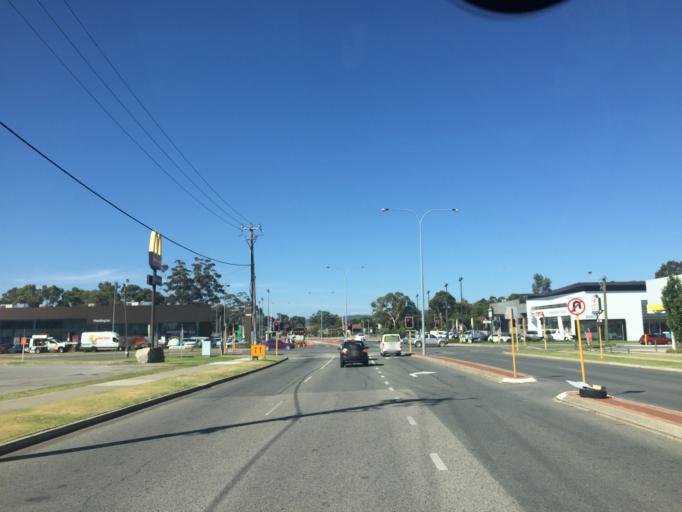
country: AU
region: Western Australia
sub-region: Gosnells
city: Maddington
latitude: -32.0517
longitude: 115.9835
